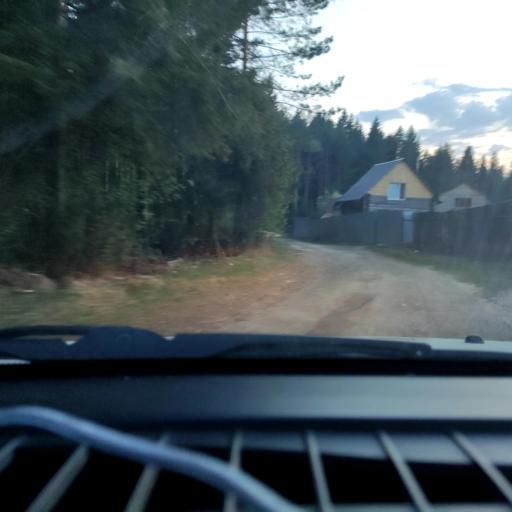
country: RU
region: Perm
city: Perm
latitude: 58.1531
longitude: 56.2949
